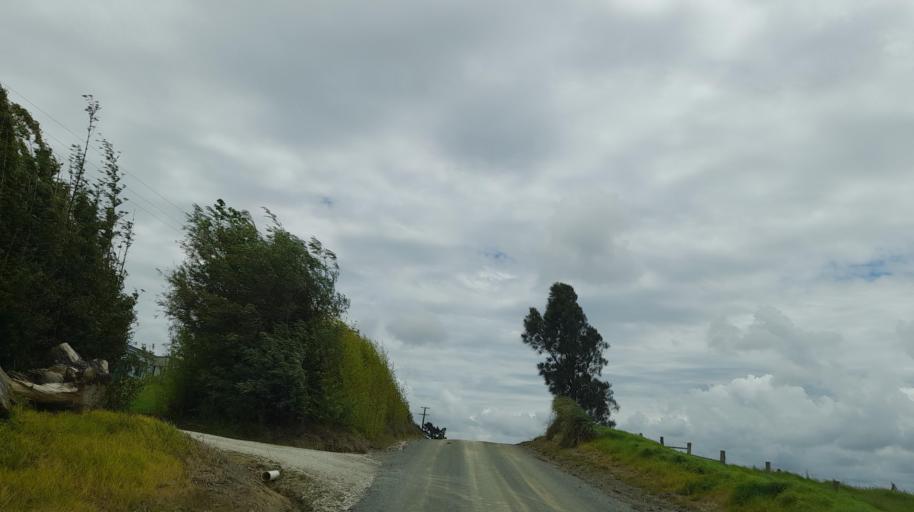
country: NZ
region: Auckland
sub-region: Auckland
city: Wellsford
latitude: -36.2672
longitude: 174.4096
